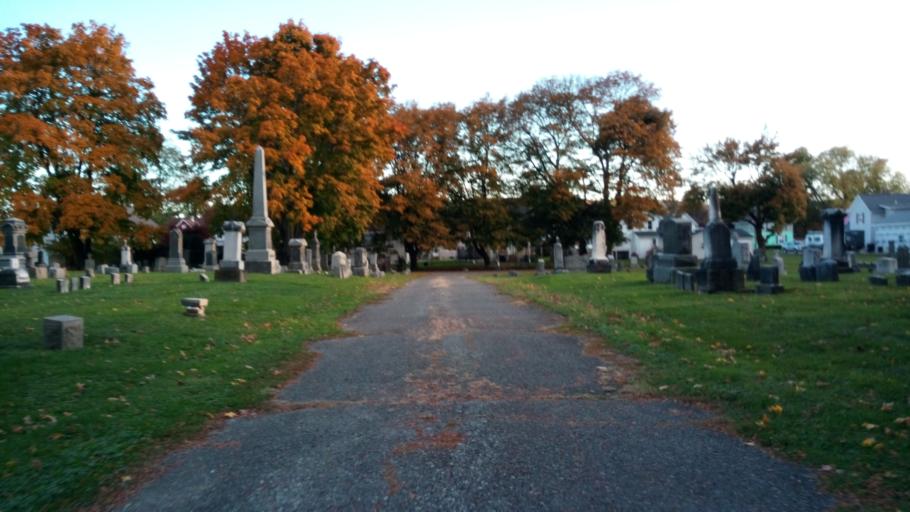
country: US
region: New York
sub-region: Chemung County
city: Southport
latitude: 42.0725
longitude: -76.8156
